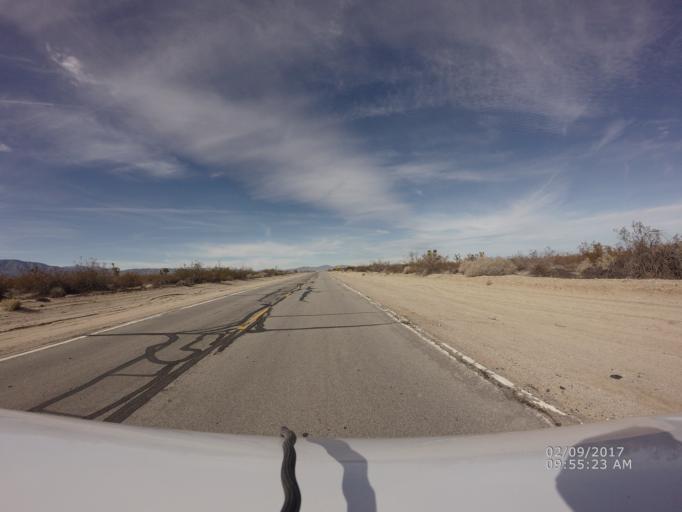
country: US
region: California
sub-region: Los Angeles County
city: Lake Los Angeles
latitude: 34.5425
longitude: -117.8393
